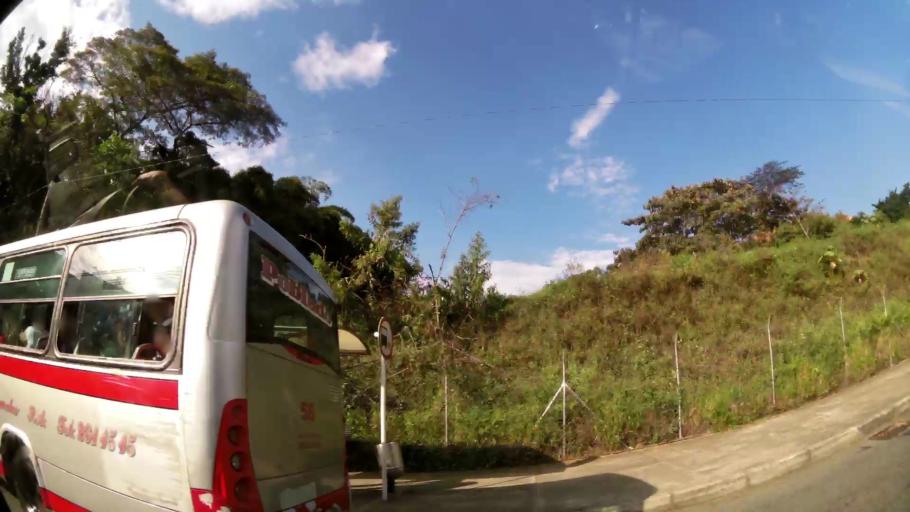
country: CO
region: Antioquia
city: Itagui
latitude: 6.2095
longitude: -75.5652
